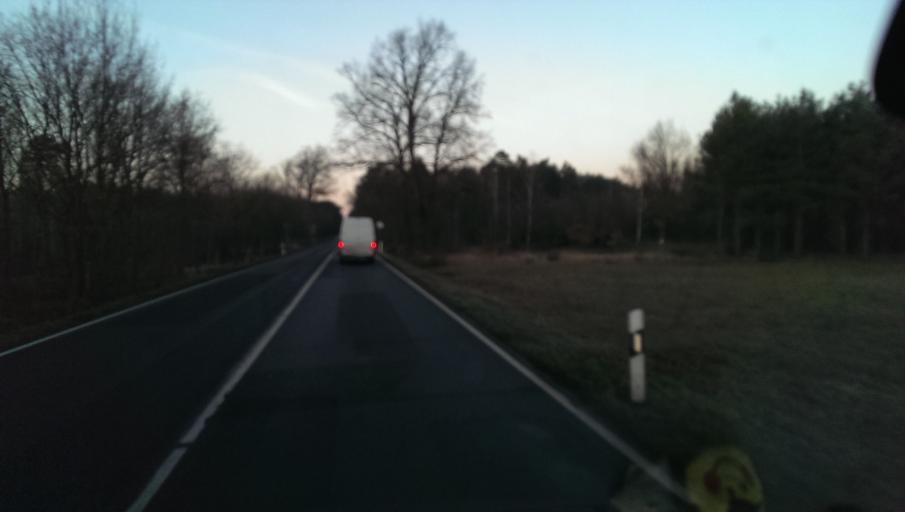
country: DE
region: Brandenburg
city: Herzberg
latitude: 51.7394
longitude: 13.2055
